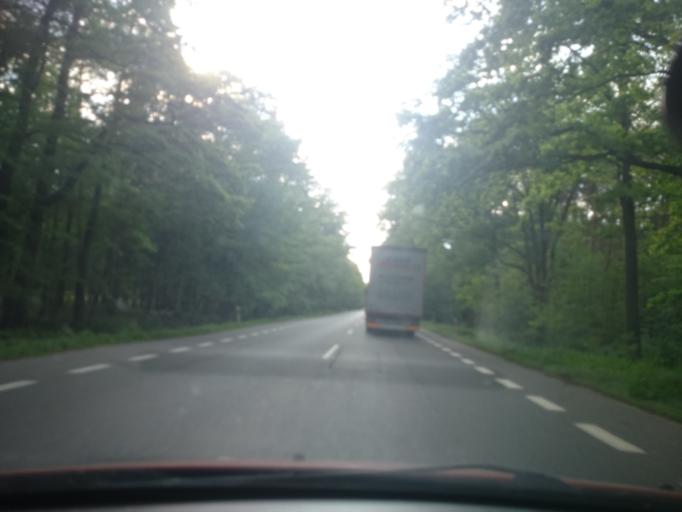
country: PL
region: Opole Voivodeship
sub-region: Powiat opolski
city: Chrzastowice
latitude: 50.6338
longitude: 18.0163
